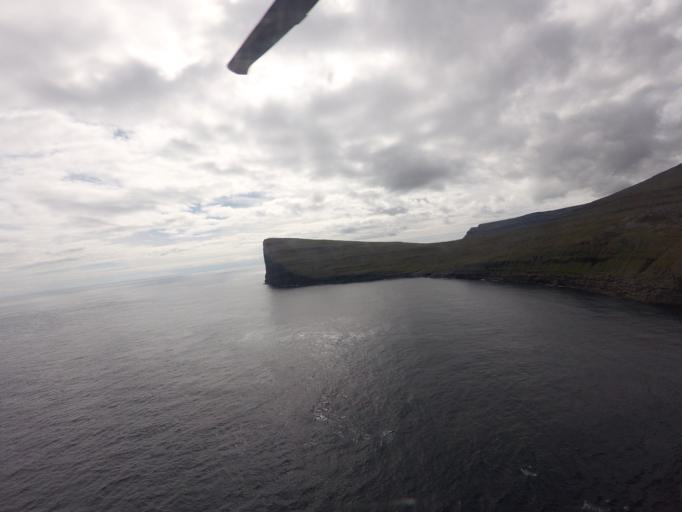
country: FO
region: Nordoyar
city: Klaksvik
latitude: 62.3087
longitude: -6.3152
